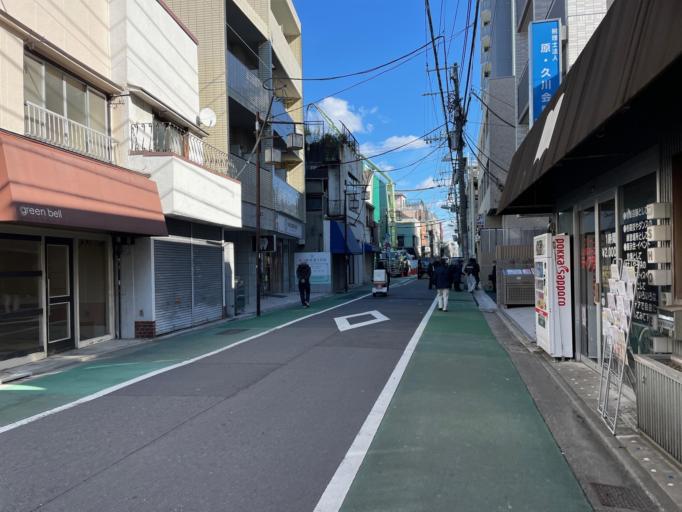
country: JP
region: Tokyo
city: Tokyo
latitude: 35.6093
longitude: 139.7114
